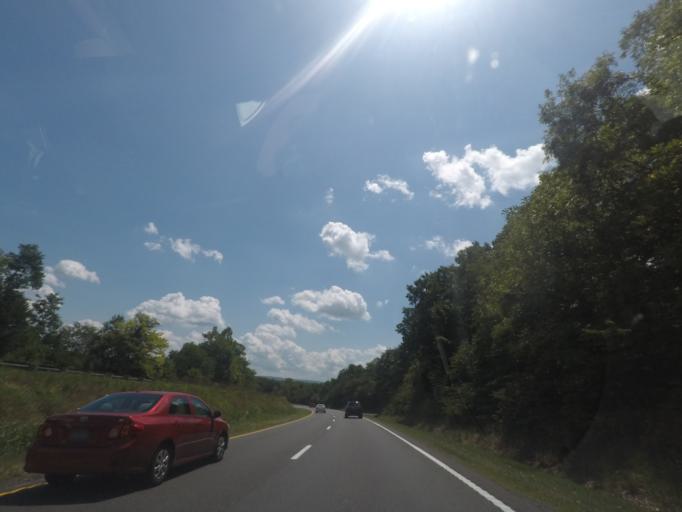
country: US
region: Virginia
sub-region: City of Winchester
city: Winchester
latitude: 39.0999
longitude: -78.1121
